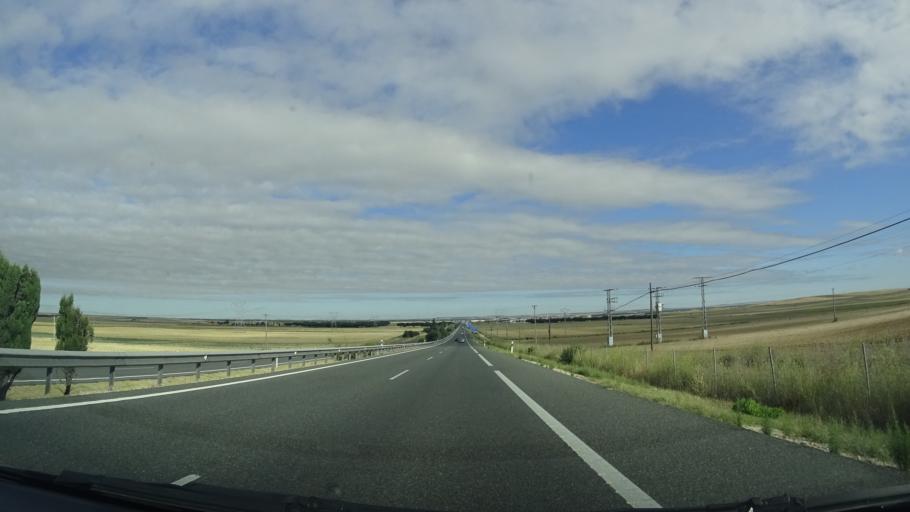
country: ES
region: Castille and Leon
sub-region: Provincia de Valladolid
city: San Vicente del Palacio
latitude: 41.2094
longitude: -4.8318
